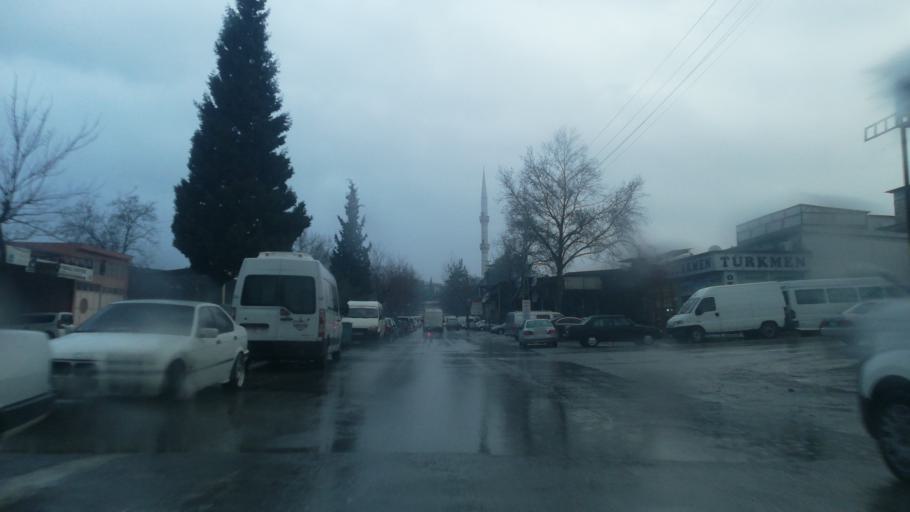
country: TR
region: Kahramanmaras
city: Kahramanmaras
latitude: 37.5637
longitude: 36.9549
